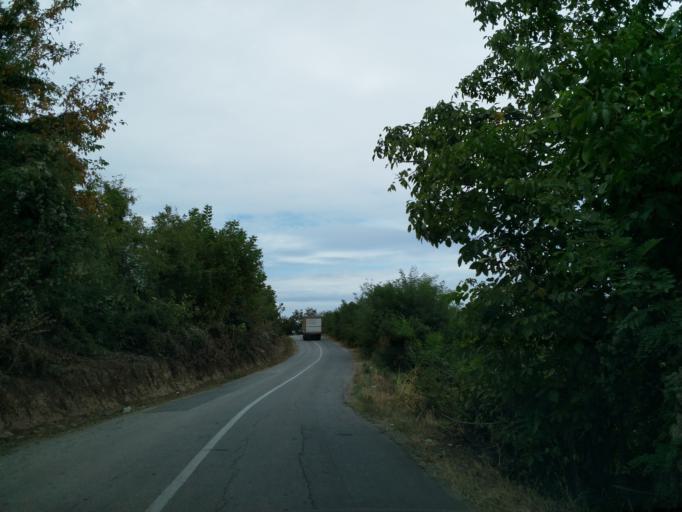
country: RS
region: Central Serbia
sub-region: Pomoravski Okrug
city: Cuprija
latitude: 43.8584
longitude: 21.3249
